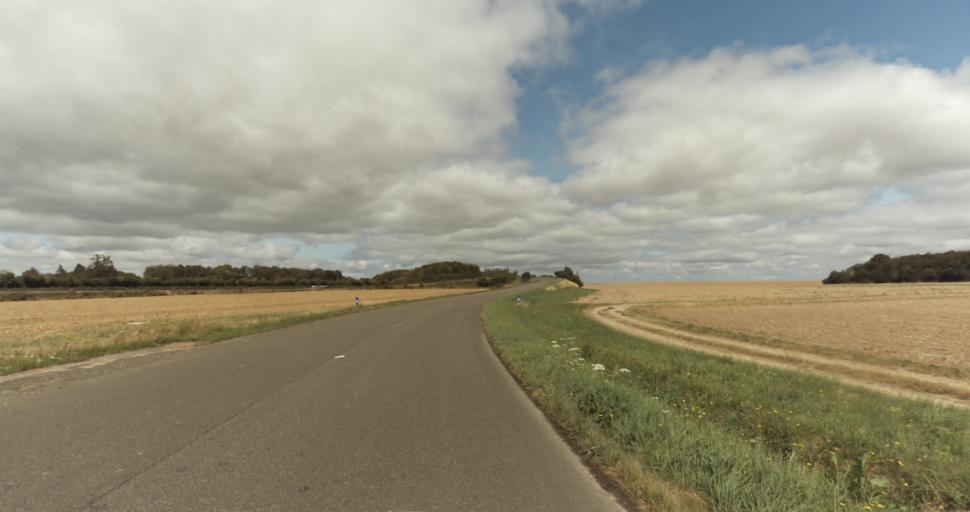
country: FR
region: Haute-Normandie
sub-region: Departement de l'Eure
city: Evreux
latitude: 48.9227
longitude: 1.2055
